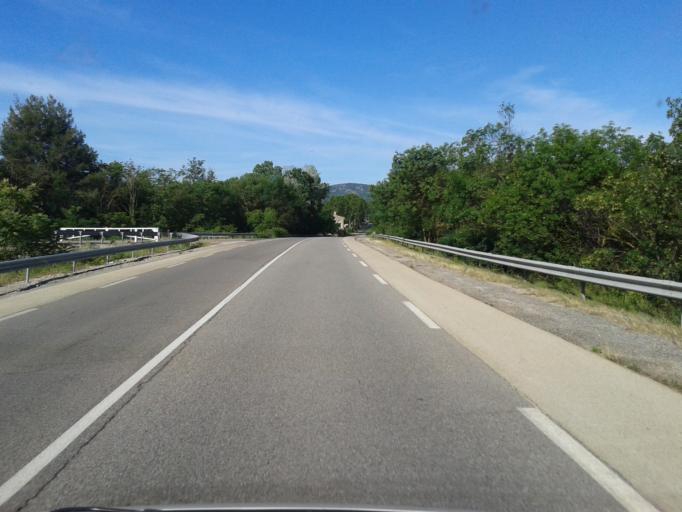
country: FR
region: Provence-Alpes-Cote d'Azur
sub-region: Departement des Bouches-du-Rhone
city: Peyrolles-en-Provence
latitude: 43.6508
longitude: 5.6074
